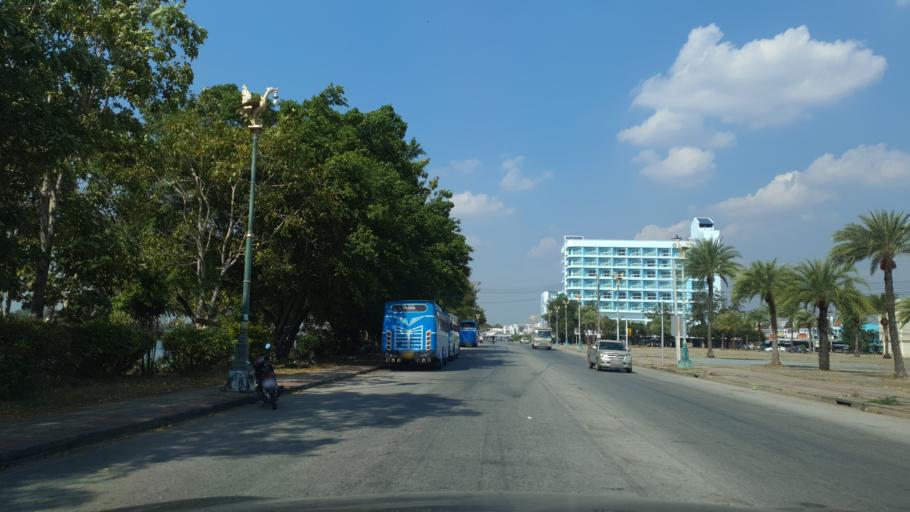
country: TH
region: Tak
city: Tak
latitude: 16.8699
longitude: 99.1234
